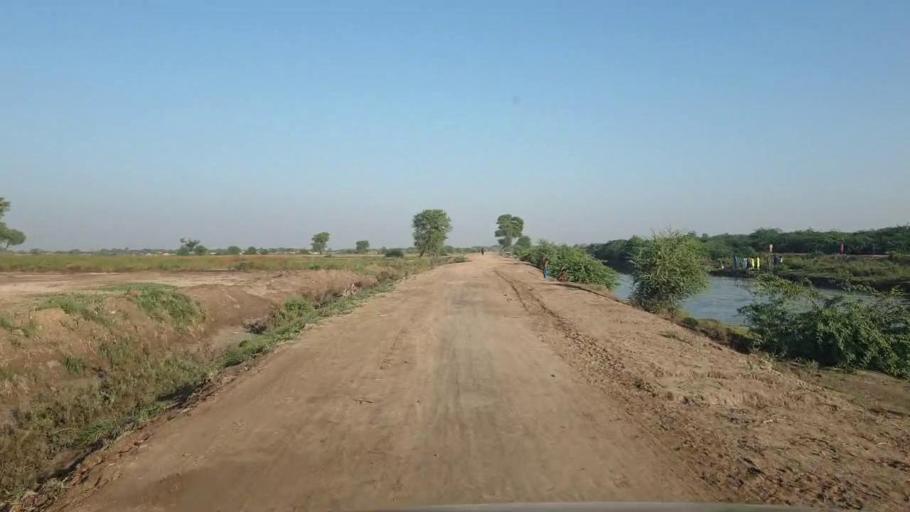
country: PK
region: Sindh
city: Badin
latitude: 24.6818
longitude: 68.8161
